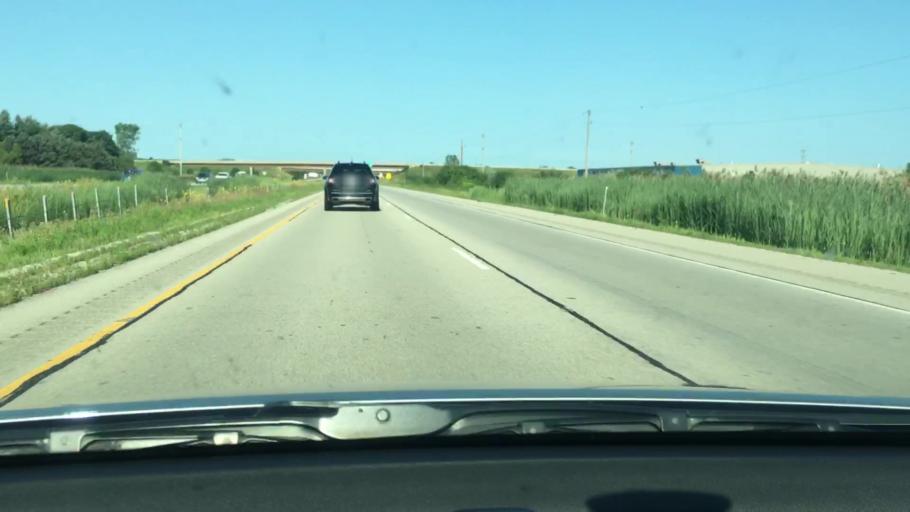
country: US
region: Wisconsin
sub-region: Outagamie County
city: Kimberly
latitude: 44.2981
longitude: -88.3489
